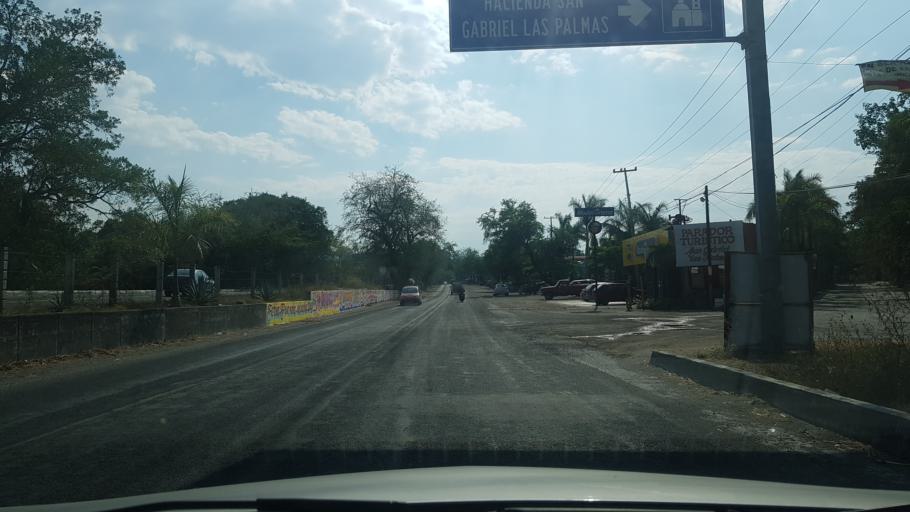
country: MX
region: Morelos
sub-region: Amacuzac
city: San Gabriel las Palmas
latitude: 18.6135
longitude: -99.3422
